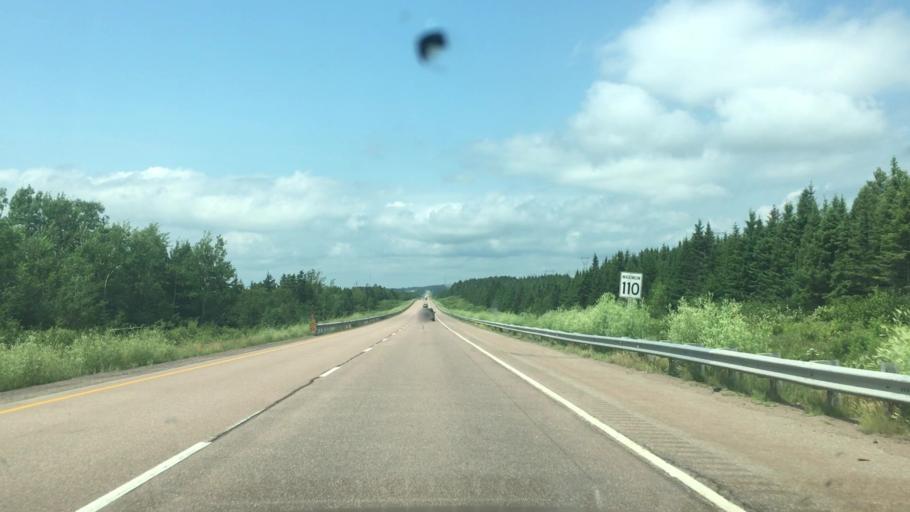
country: CA
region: New Brunswick
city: Sackville
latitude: 45.9729
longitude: -64.4406
